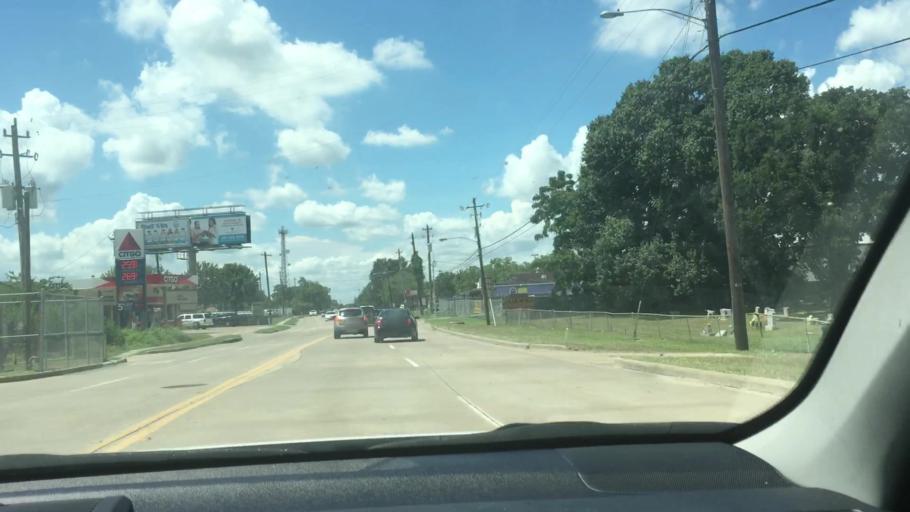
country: US
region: Texas
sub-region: Fort Bend County
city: Fifth Street
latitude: 29.6000
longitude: -95.5537
